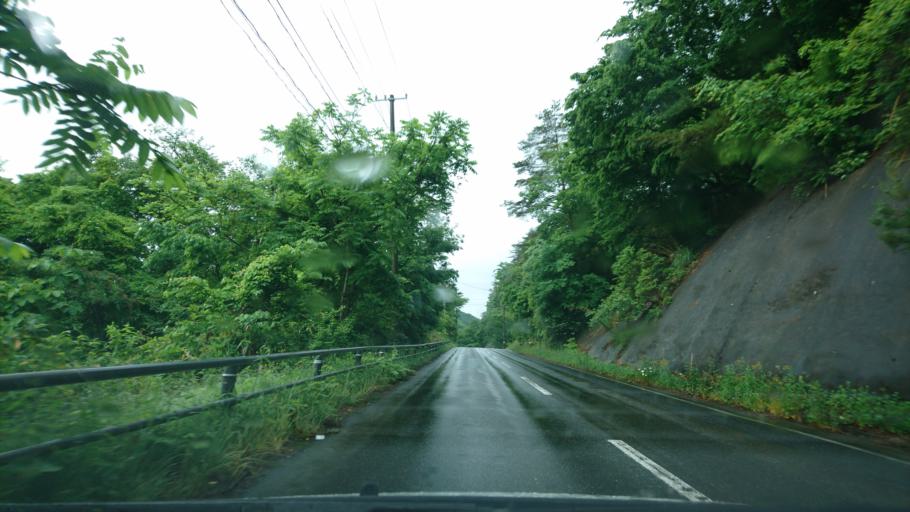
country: JP
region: Iwate
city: Ichinoseki
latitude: 38.9739
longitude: 140.9837
